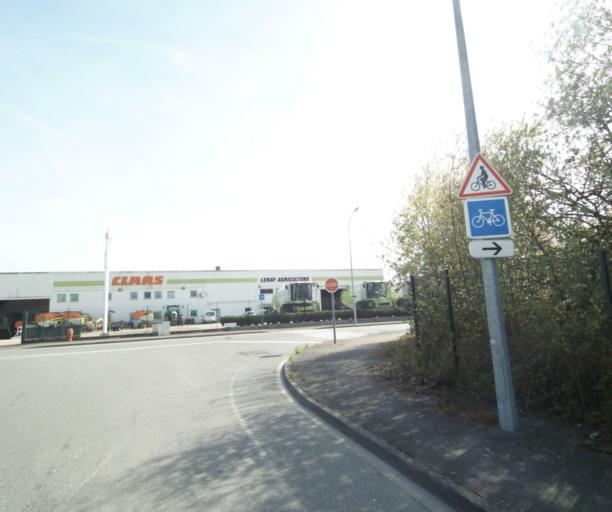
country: FR
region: Ile-de-France
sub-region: Departement de Seine-et-Marne
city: Nangis
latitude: 48.5605
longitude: 3.0347
